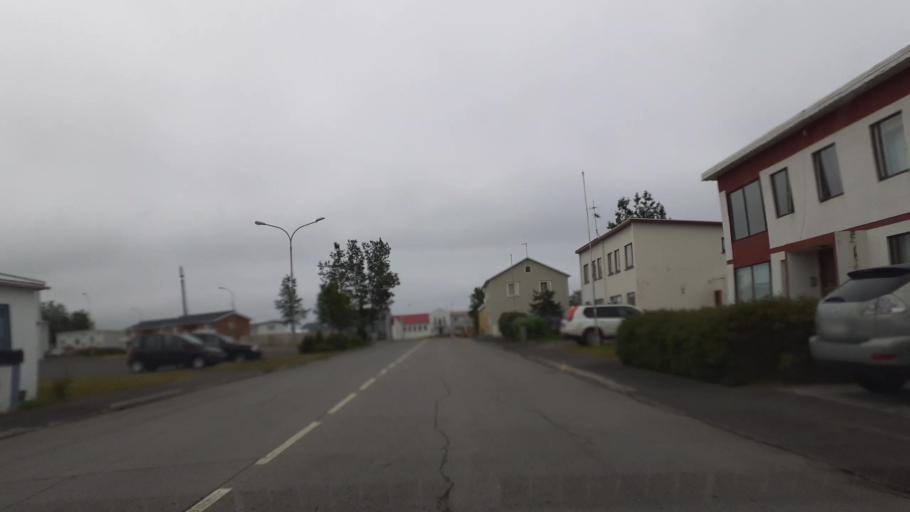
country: IS
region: Northeast
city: Dalvik
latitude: 65.9680
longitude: -18.5290
